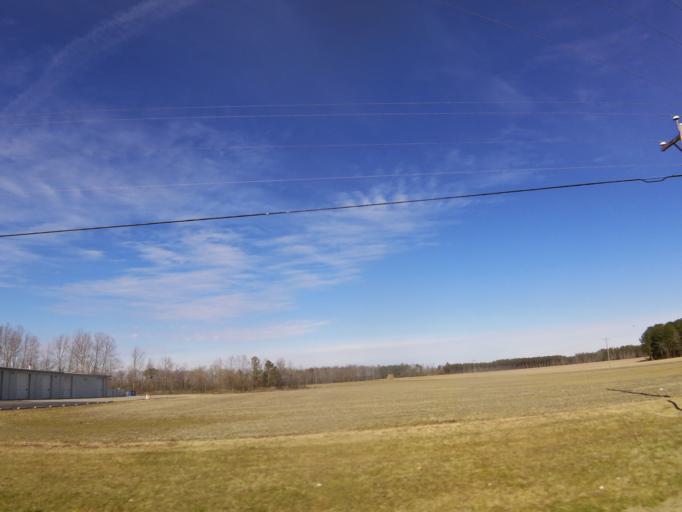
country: US
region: Virginia
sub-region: Isle of Wight County
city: Windsor
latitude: 36.7897
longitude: -76.7826
